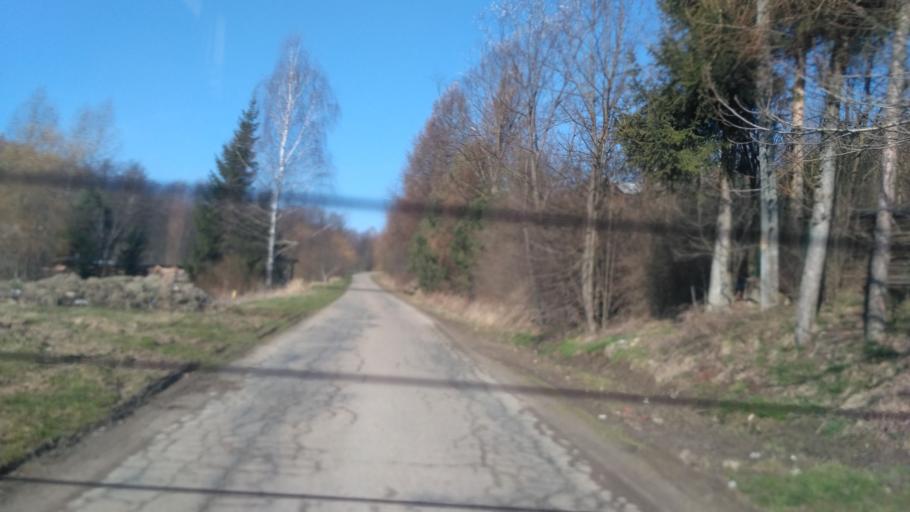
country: PL
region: Subcarpathian Voivodeship
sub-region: Powiat strzyzowski
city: Gwoznica Gorna
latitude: 49.8174
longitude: 22.0226
